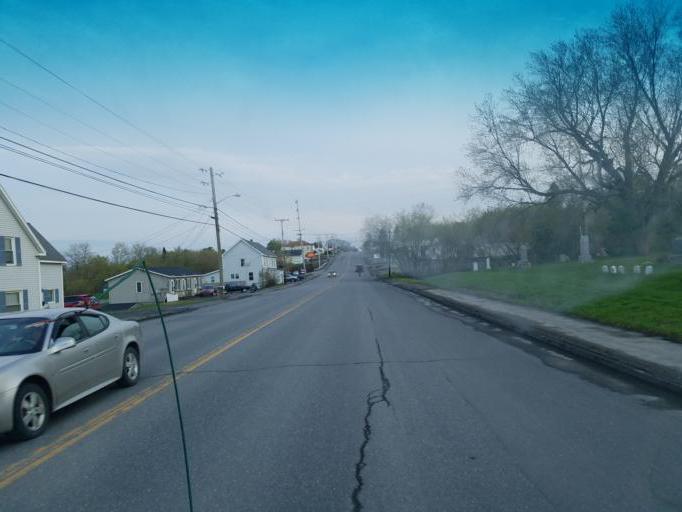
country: US
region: Maine
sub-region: Aroostook County
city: Caribou
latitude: 46.8517
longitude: -68.0111
